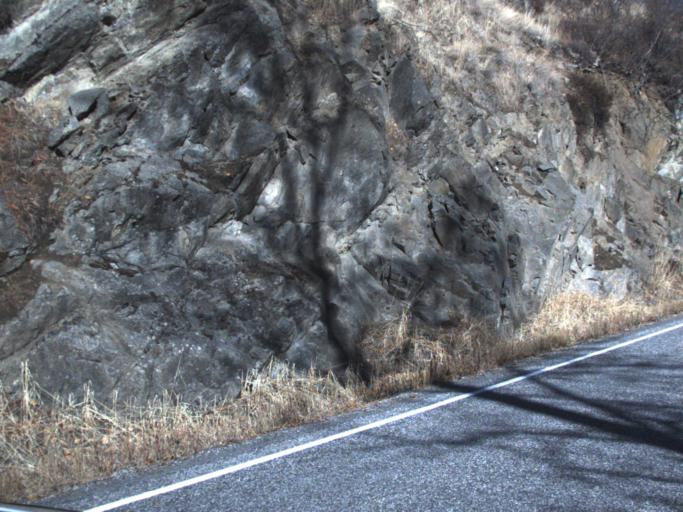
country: CA
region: British Columbia
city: Grand Forks
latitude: 48.9285
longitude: -118.5659
